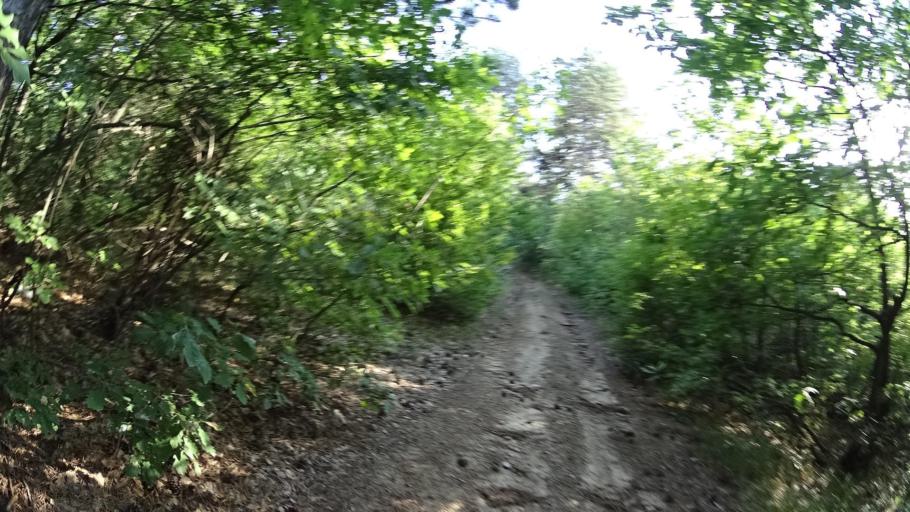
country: BG
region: Plovdiv
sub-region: Obshtina Plovdiv
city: Plovdiv
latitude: 42.0563
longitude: 24.6862
